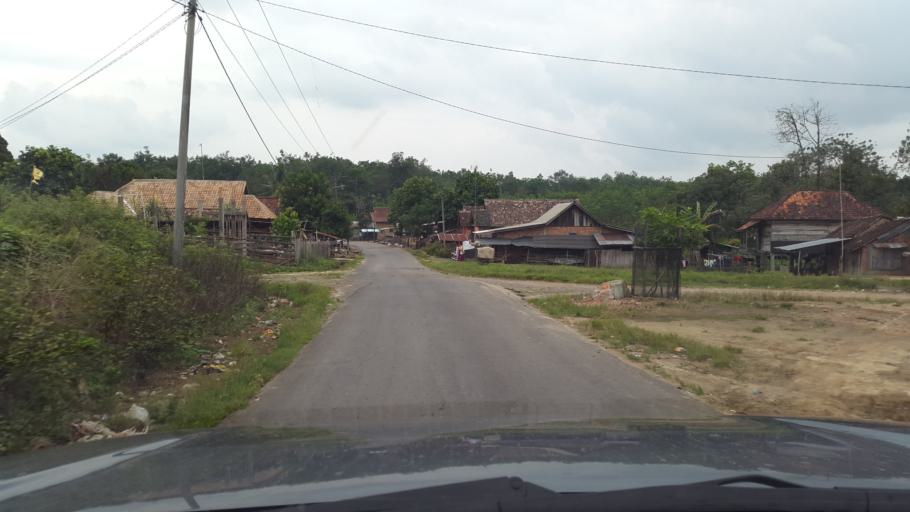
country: ID
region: South Sumatra
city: Gunungmenang
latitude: -3.1697
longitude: 103.9905
